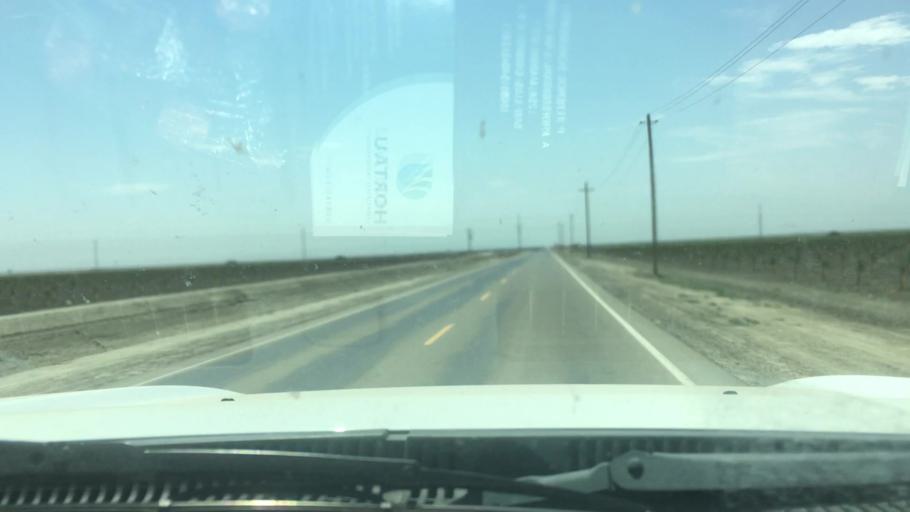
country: US
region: California
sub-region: Kings County
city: Corcoran
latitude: 36.0508
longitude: -119.5675
